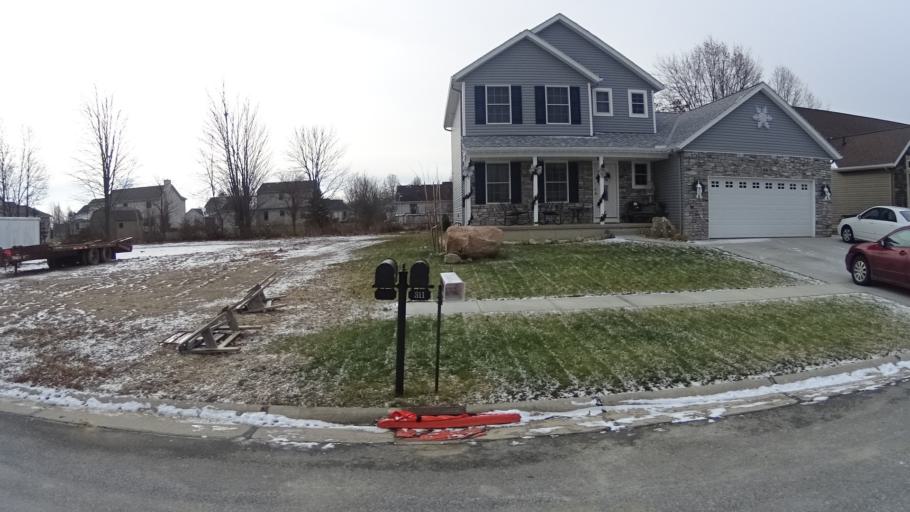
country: US
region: Ohio
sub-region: Lorain County
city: Lagrange
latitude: 41.2452
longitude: -82.1122
